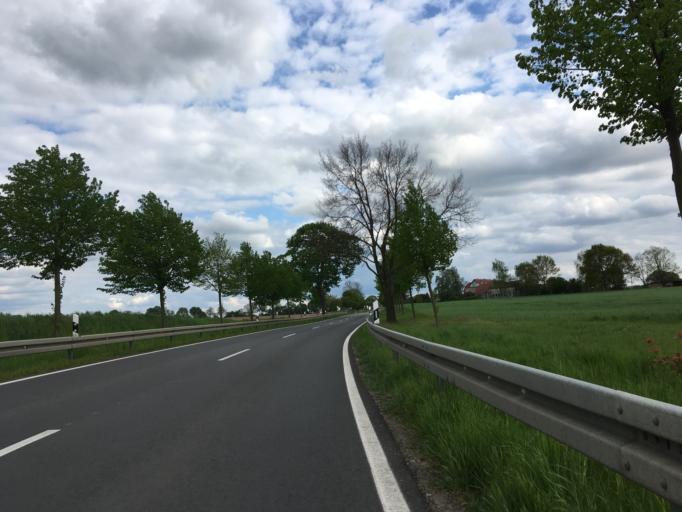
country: DE
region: Brandenburg
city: Bernau bei Berlin
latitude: 52.6599
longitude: 13.5984
